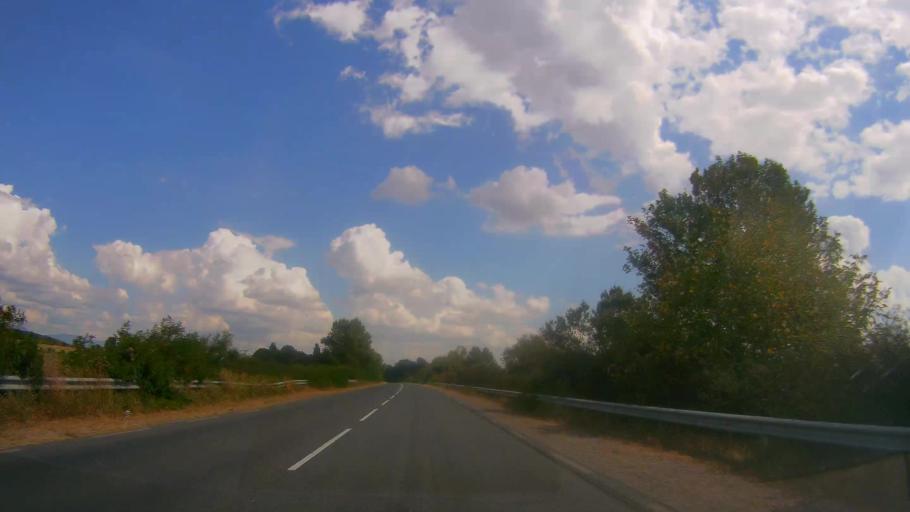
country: BG
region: Sliven
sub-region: Obshtina Sliven
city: Kermen
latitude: 42.6318
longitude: 26.1739
